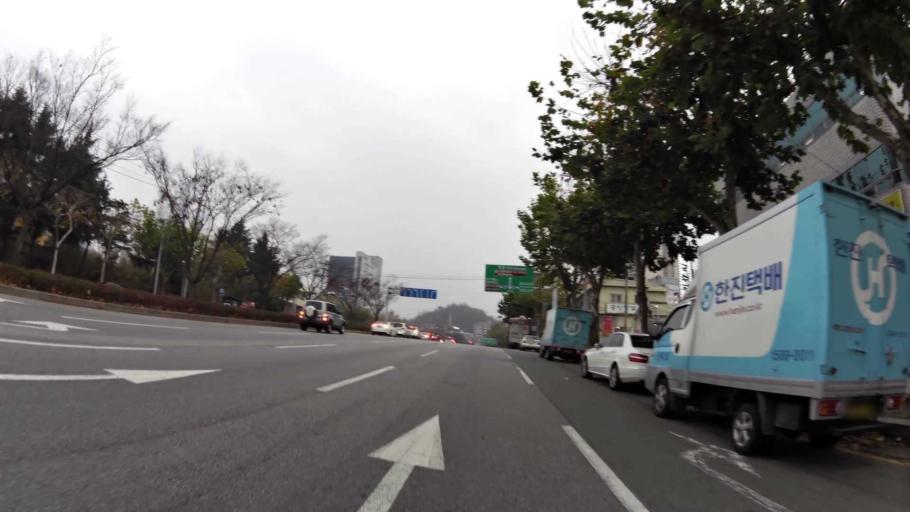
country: KR
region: Daegu
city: Daegu
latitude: 35.8606
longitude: 128.6474
